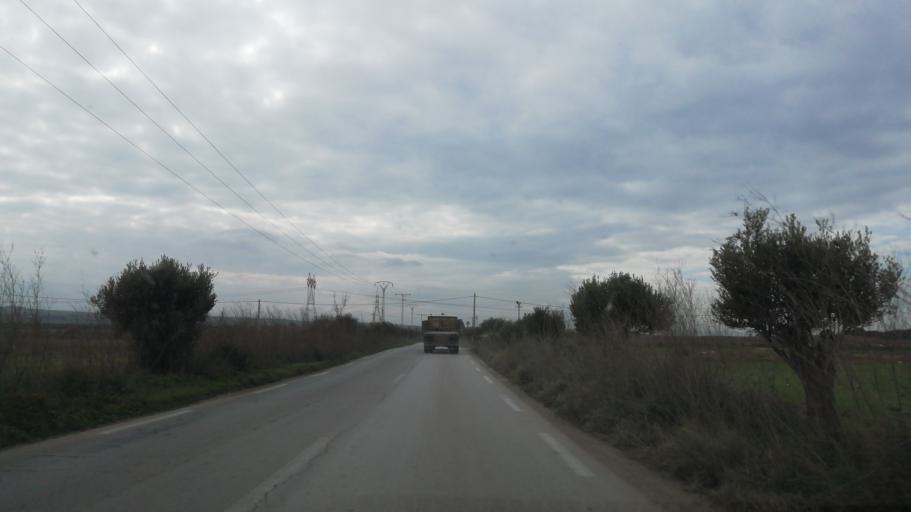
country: DZ
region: Oran
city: Ain el Bya
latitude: 35.7769
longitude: -0.3457
